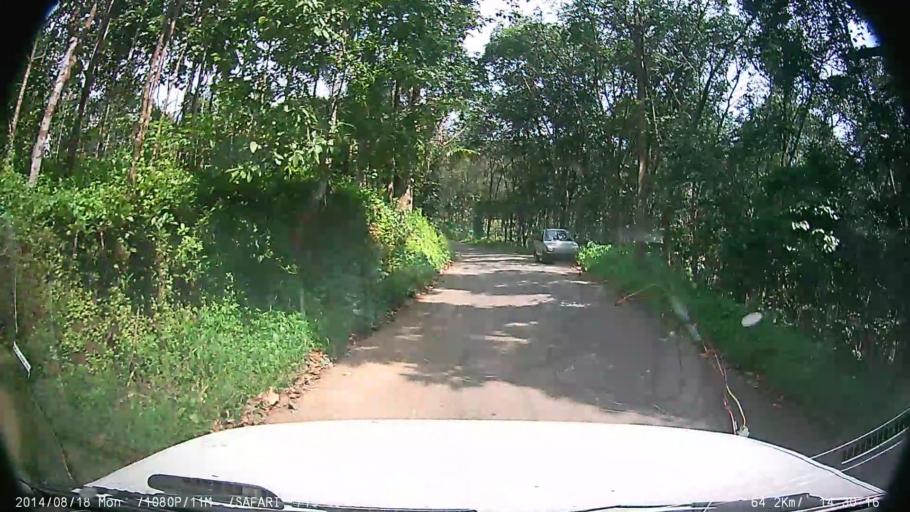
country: IN
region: Kerala
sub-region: Kottayam
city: Palackattumala
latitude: 9.7887
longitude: 76.5501
